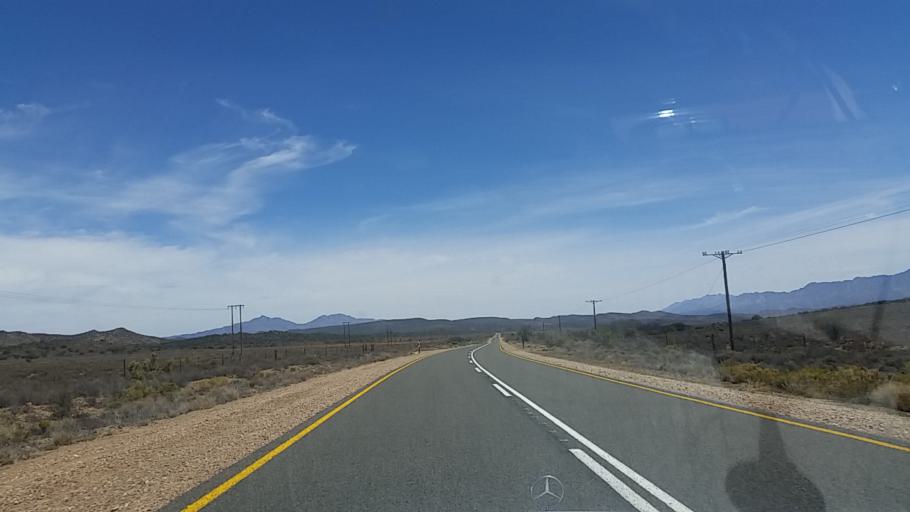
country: ZA
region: Eastern Cape
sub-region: Cacadu District Municipality
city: Willowmore
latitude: -33.5012
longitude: 23.2590
